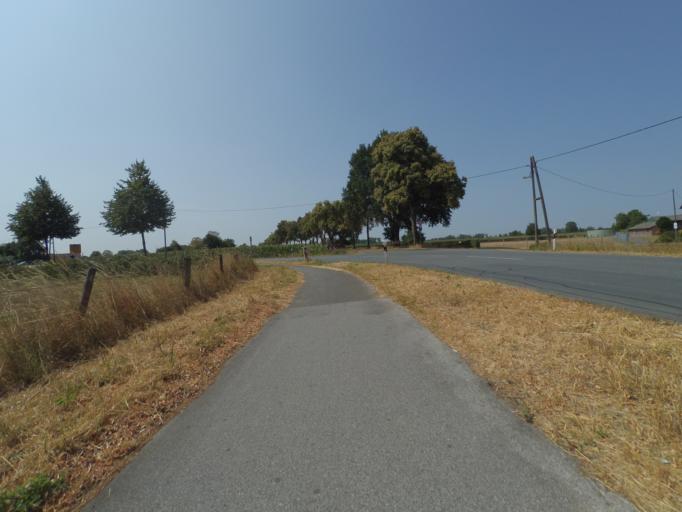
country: DE
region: North Rhine-Westphalia
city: Rees
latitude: 51.7940
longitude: 6.4133
